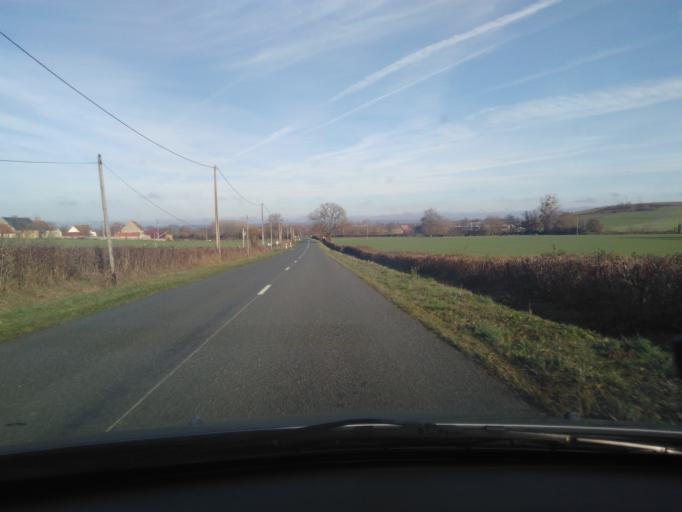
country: FR
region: Centre
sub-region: Departement du Cher
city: Orval
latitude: 46.6835
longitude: 2.4640
